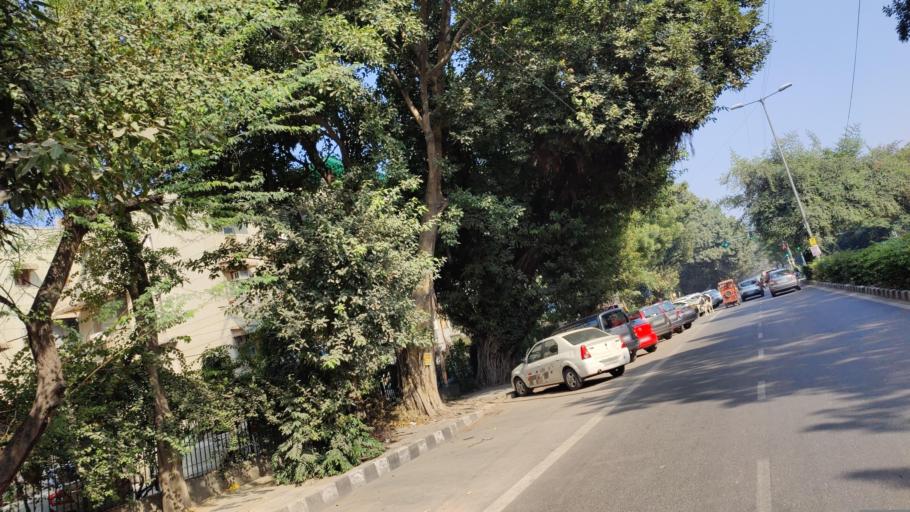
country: IN
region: NCT
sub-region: North West Delhi
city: Pitampura
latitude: 28.7111
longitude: 77.1270
